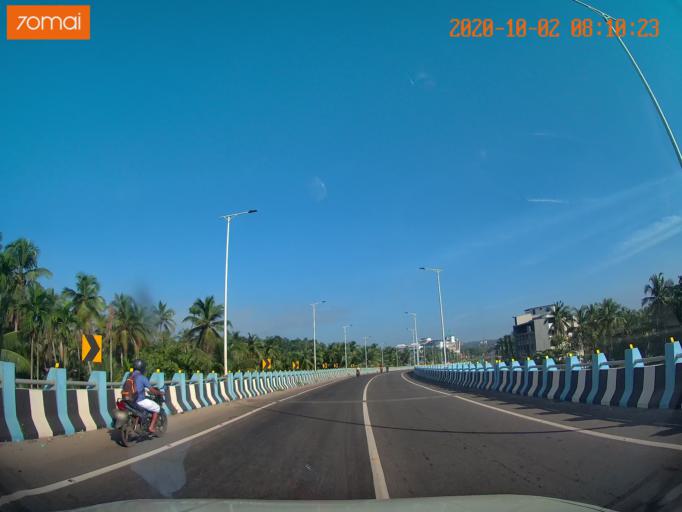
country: IN
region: Kerala
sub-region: Kozhikode
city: Kozhikode
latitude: 11.2652
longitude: 75.8112
